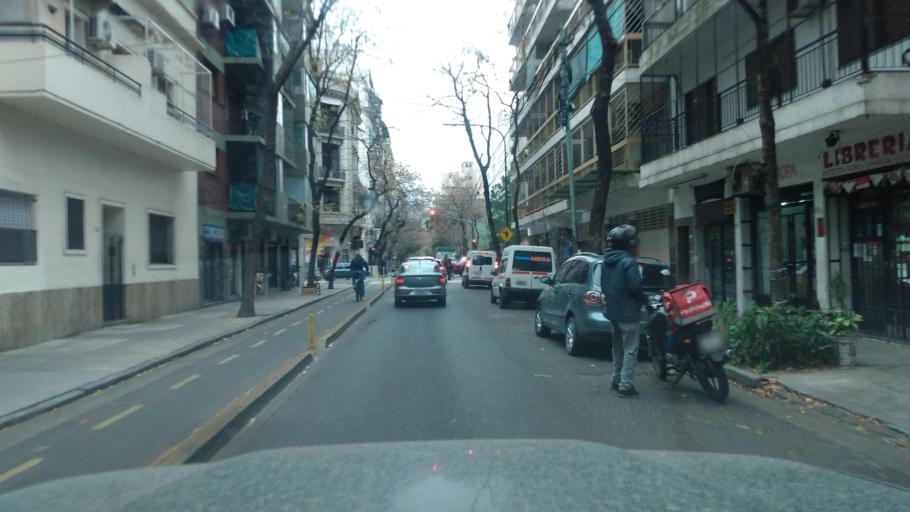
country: AR
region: Buenos Aires F.D.
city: Buenos Aires
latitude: -34.6125
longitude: -58.3962
